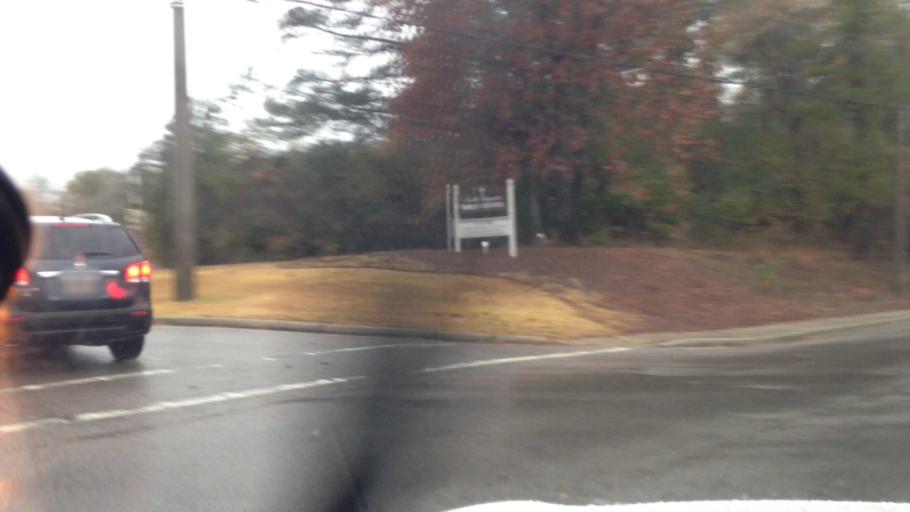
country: US
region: South Carolina
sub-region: Aiken County
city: North Augusta
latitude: 33.5108
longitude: -81.9754
